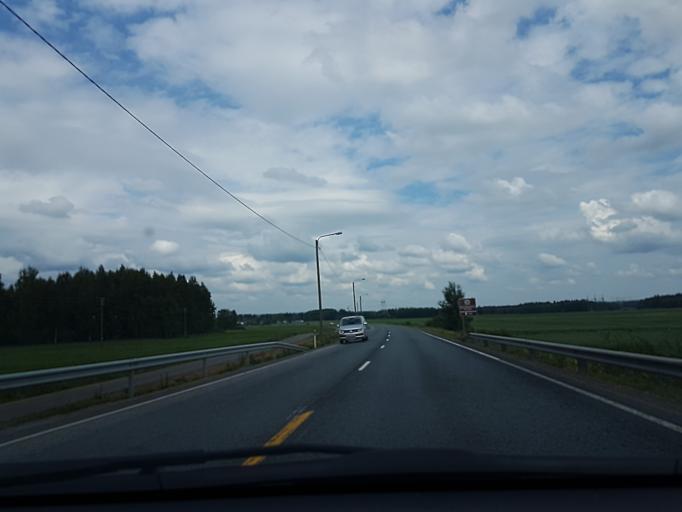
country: FI
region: Uusimaa
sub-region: Helsinki
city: Jaervenpaeae
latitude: 60.5091
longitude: 25.1010
